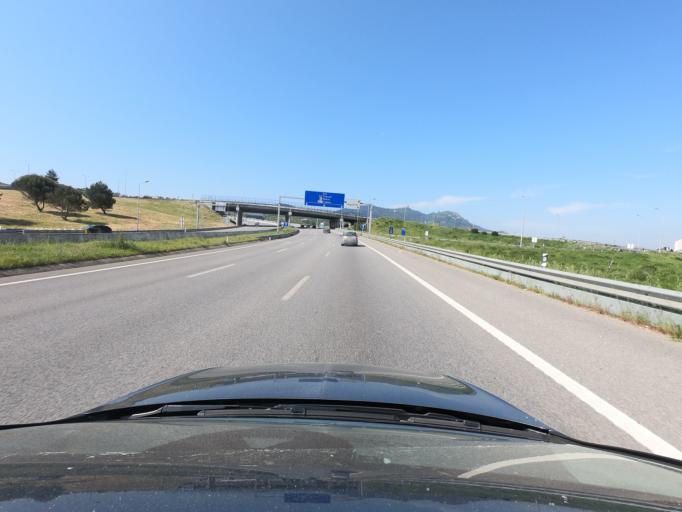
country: PT
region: Lisbon
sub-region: Sintra
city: Sintra
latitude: 38.8049
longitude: -9.3615
